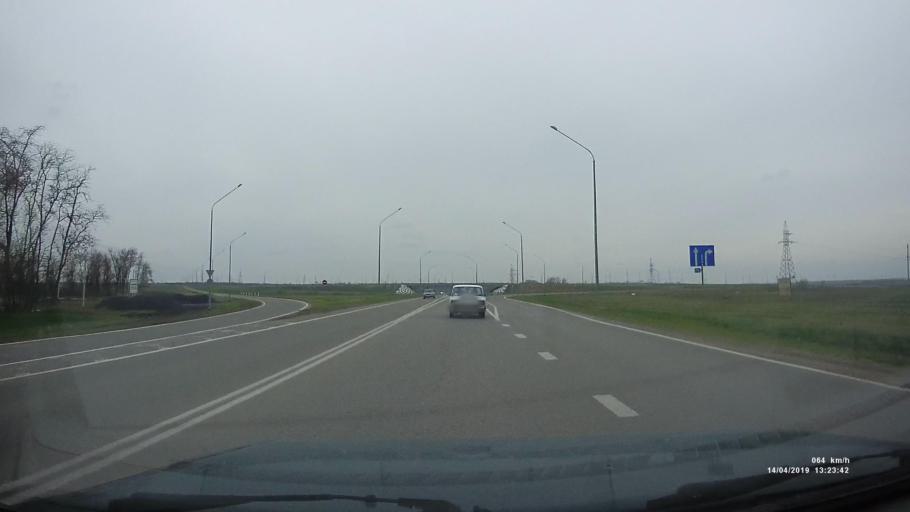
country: RU
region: Rostov
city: Kuleshovka
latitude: 47.0839
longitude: 39.4967
